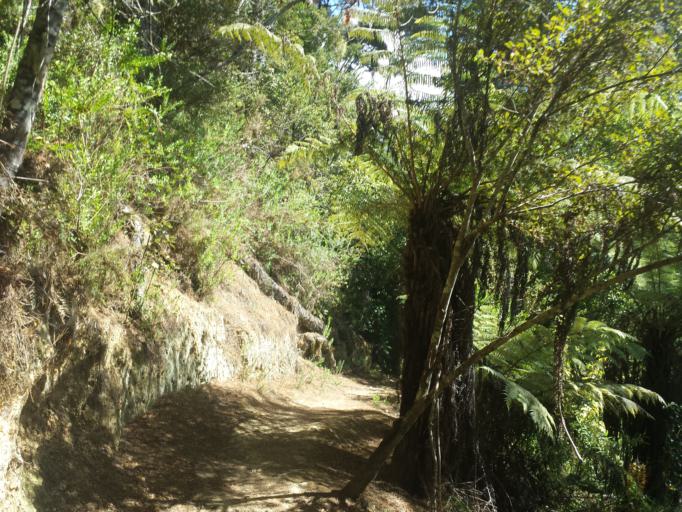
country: NZ
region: Northland
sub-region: Far North District
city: Paihia
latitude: -35.3043
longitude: 174.1032
